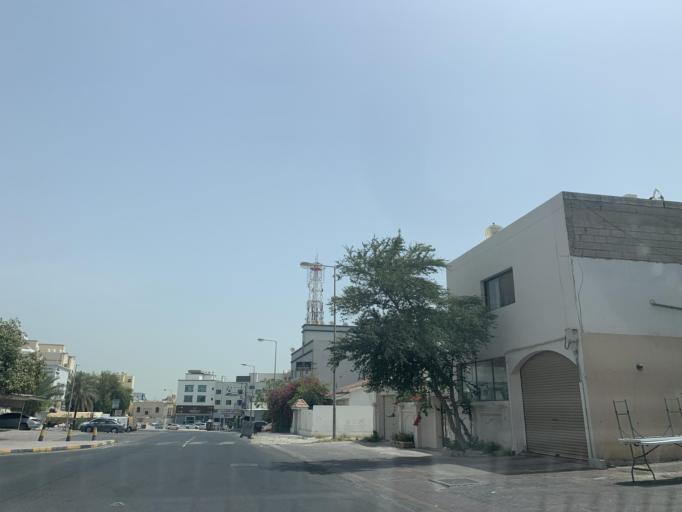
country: BH
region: Northern
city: Ar Rifa'
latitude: 26.1306
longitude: 50.5771
